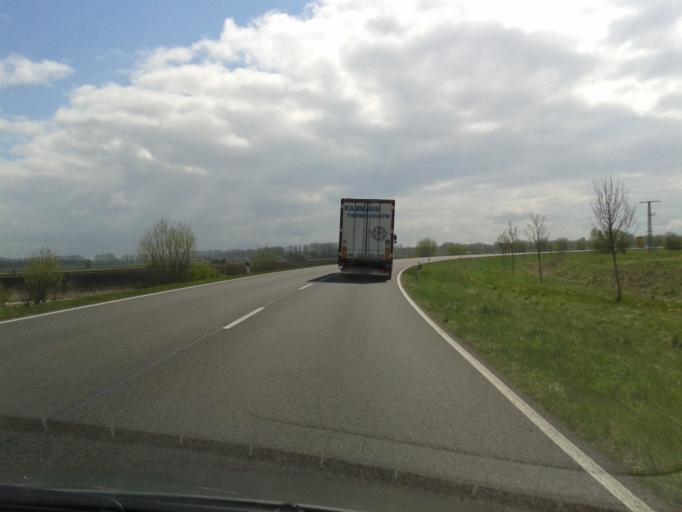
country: DE
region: Saxony-Anhalt
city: Salzwedel
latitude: 52.8654
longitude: 11.1756
